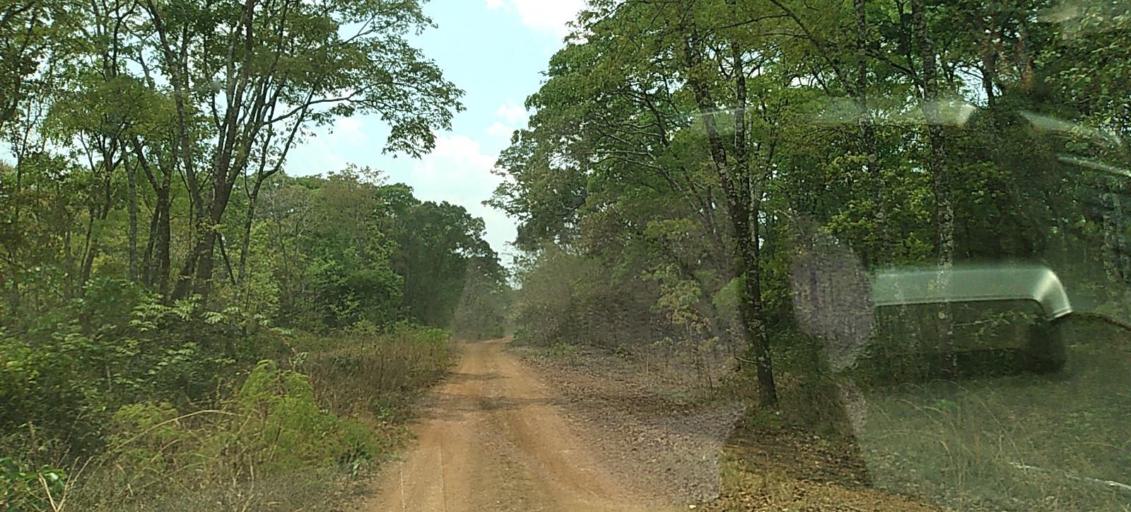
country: ZM
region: Copperbelt
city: Chingola
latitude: -12.8013
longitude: 27.6432
